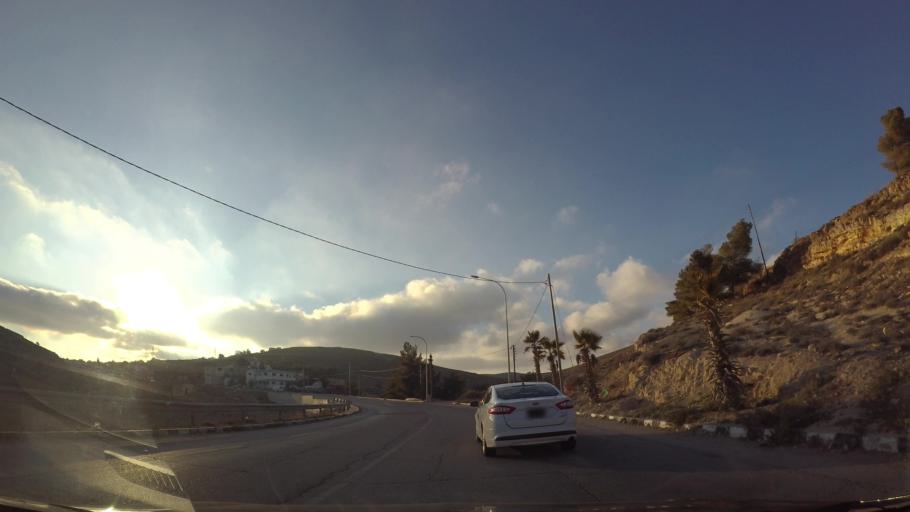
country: JO
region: Ma'an
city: Petra
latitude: 30.5217
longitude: 35.5509
